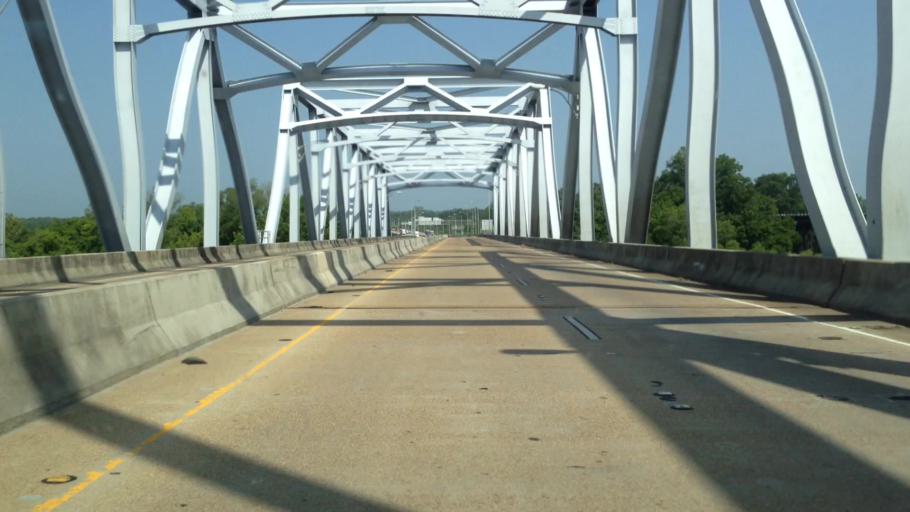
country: US
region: Mississippi
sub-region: Warren County
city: Vicksburg
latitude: 32.3158
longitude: -90.9095
